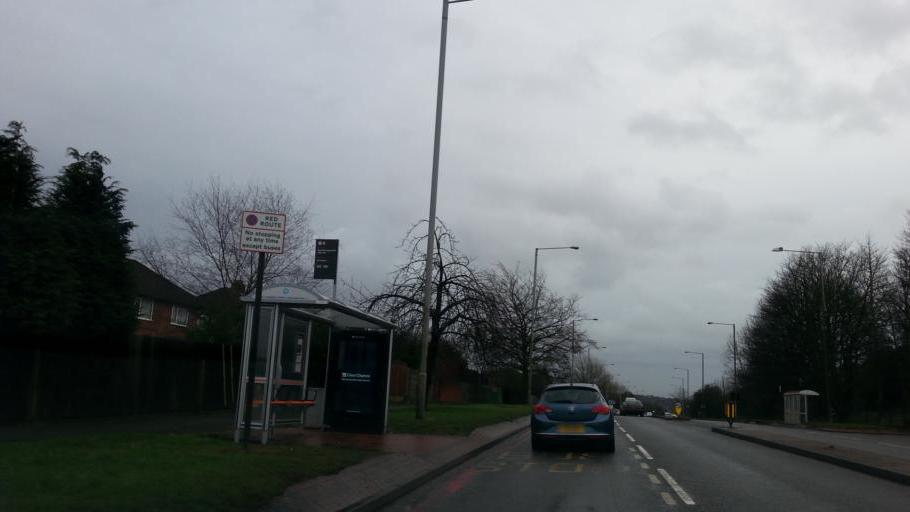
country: GB
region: England
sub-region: Sandwell
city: Oldbury
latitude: 52.5065
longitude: -2.0373
